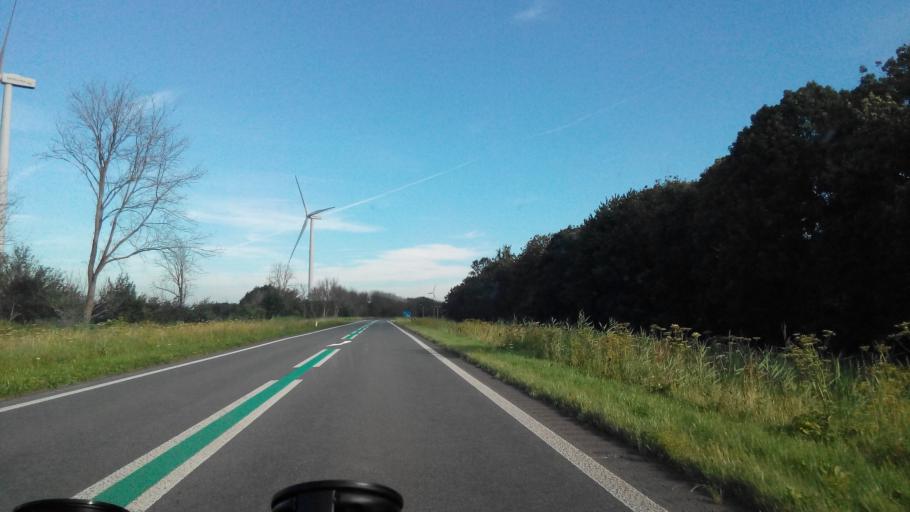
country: NL
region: Utrecht
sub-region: Gemeente Bunschoten
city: Bunschoten
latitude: 52.3157
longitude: 5.4392
